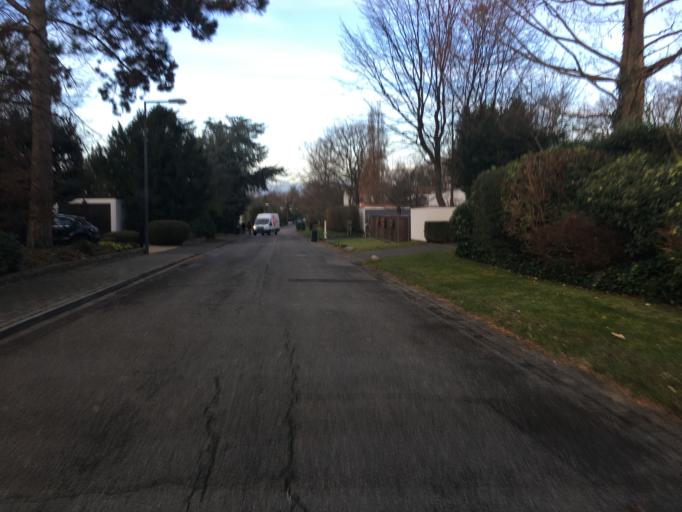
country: DE
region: North Rhine-Westphalia
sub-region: Regierungsbezirk Koln
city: Bayenthal
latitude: 50.8716
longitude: 6.9778
